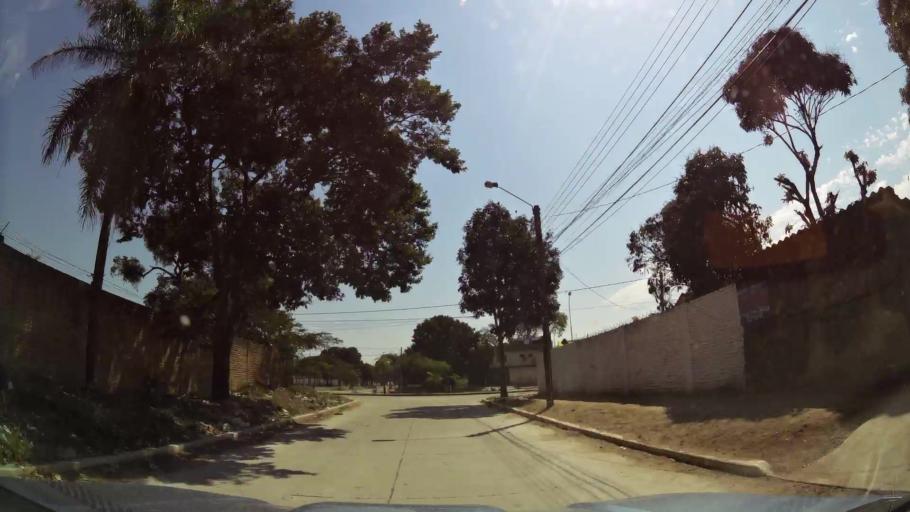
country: BO
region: Santa Cruz
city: Santa Cruz de la Sierra
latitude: -17.7399
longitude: -63.1564
